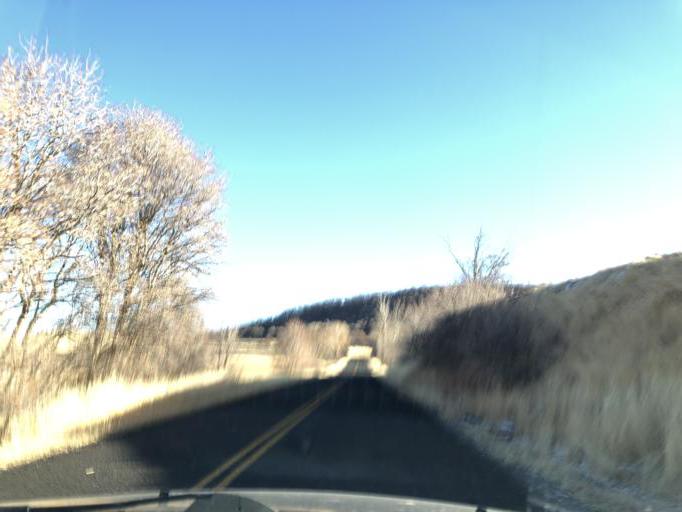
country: US
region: Utah
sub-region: Cache County
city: Wellsville
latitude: 41.5805
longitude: -111.9236
